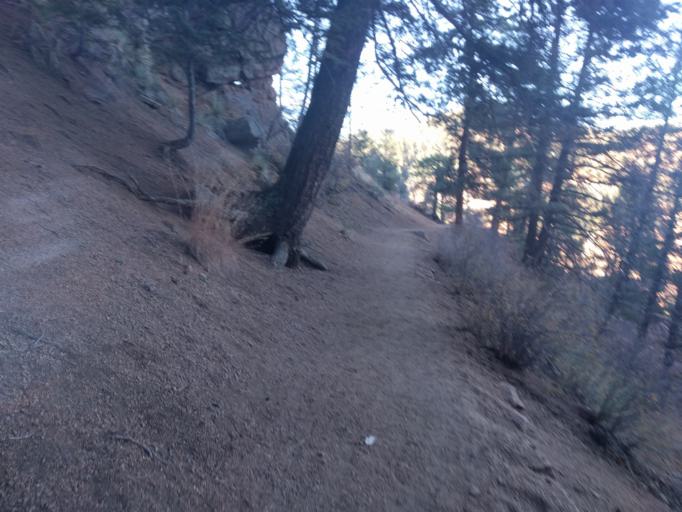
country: US
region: Colorado
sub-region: El Paso County
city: Colorado Springs
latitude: 38.7893
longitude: -104.8805
